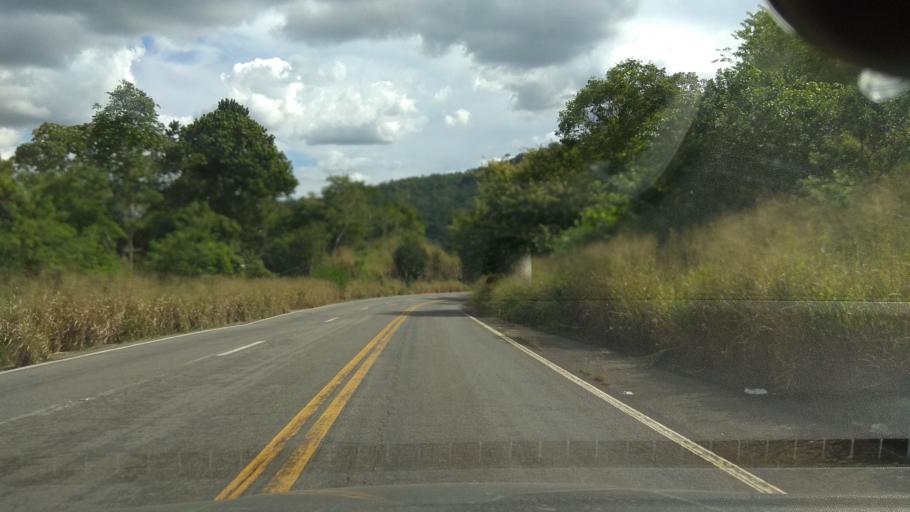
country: BR
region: Bahia
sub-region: Ubaitaba
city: Ubaitaba
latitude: -14.2528
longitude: -39.3727
